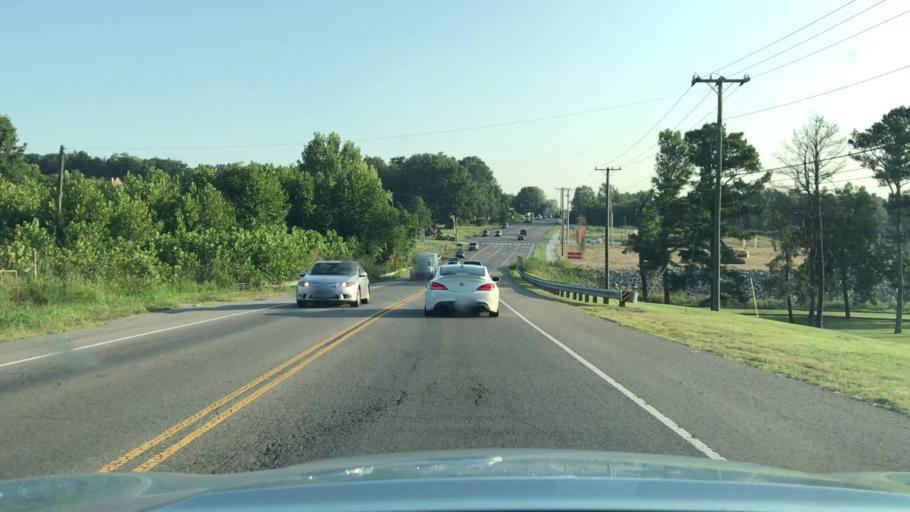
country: US
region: Tennessee
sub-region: Rutherford County
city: La Vergne
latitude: 36.0070
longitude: -86.6217
